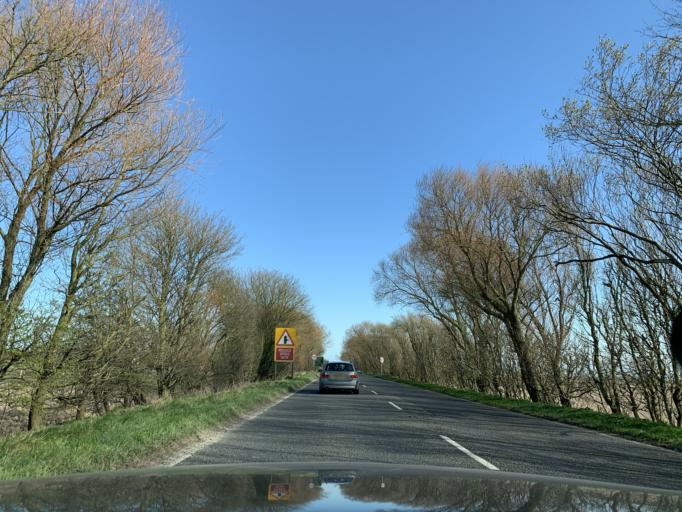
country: GB
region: England
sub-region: Kent
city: New Romney
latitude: 50.9860
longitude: 0.9155
